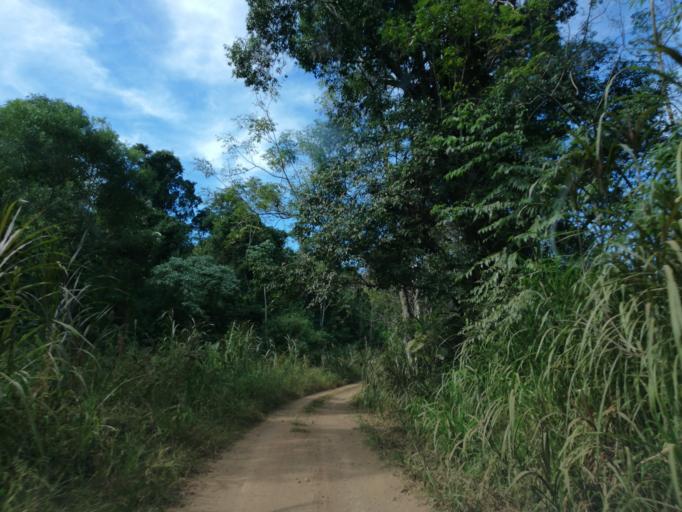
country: AR
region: Misiones
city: Dos de Mayo
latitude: -27.0143
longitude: -54.4349
